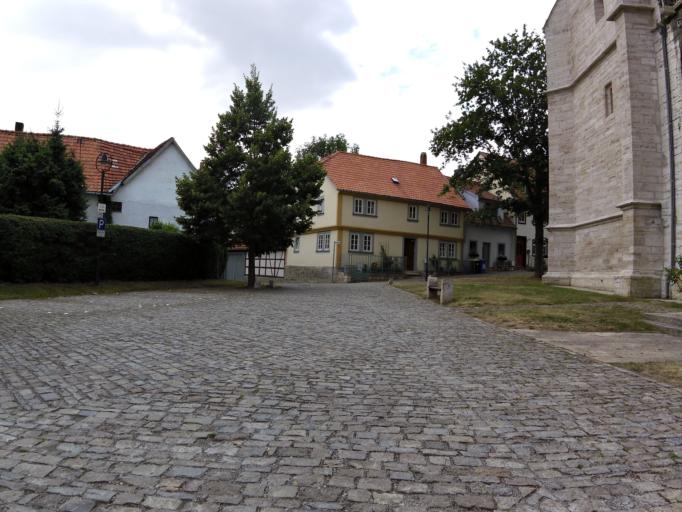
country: DE
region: Thuringia
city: Bad Langensalza
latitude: 51.1108
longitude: 10.6452
